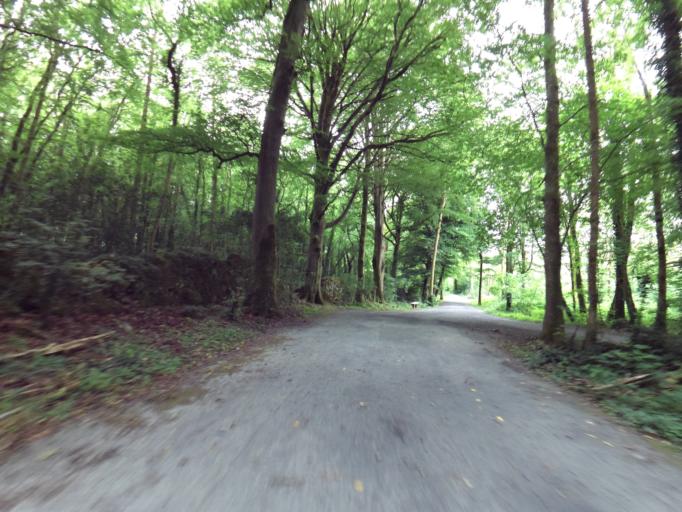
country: IE
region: Connaught
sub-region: County Galway
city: Gort
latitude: 53.0833
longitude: -8.8437
